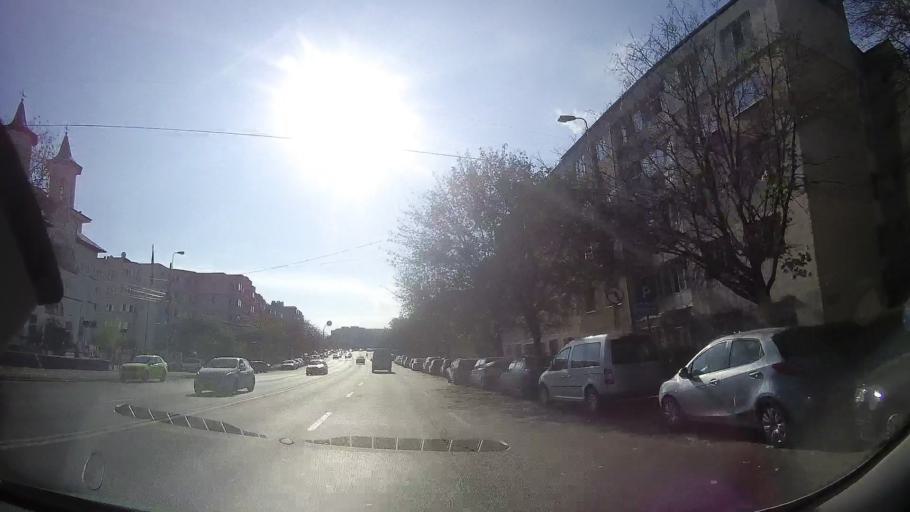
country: RO
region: Constanta
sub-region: Municipiul Constanta
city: Constanta
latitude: 44.1595
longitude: 28.6316
